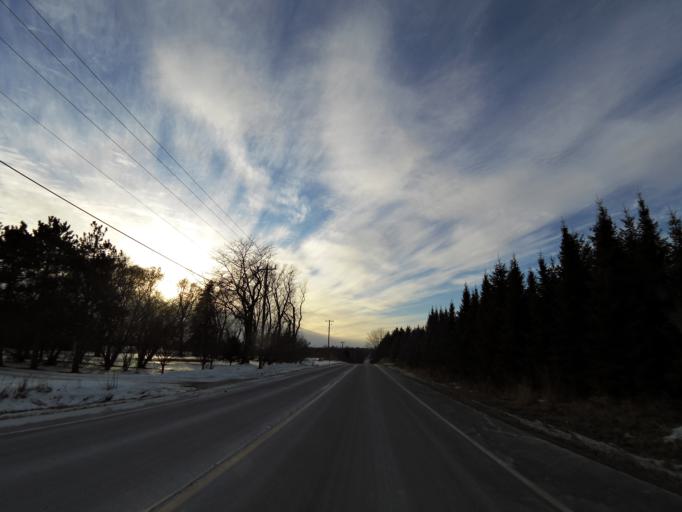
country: US
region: Minnesota
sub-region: Washington County
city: Afton
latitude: 44.8909
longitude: -92.8308
